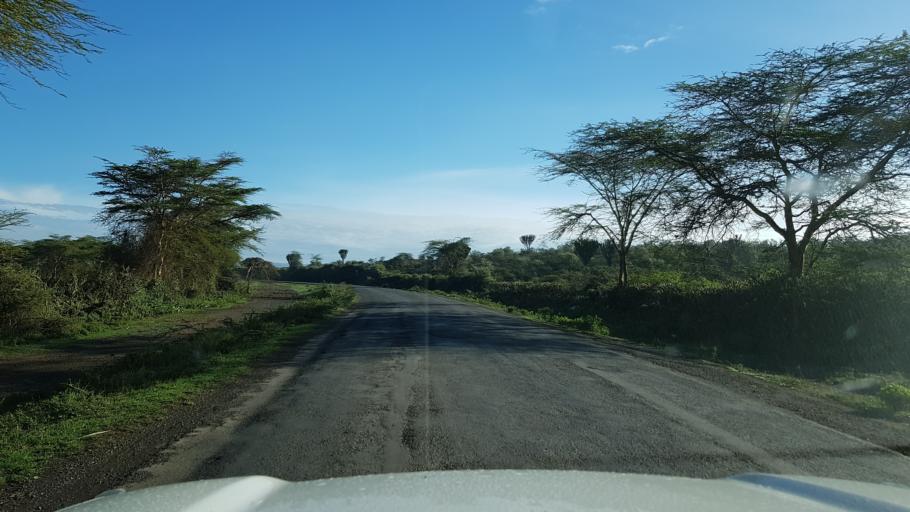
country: KE
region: Nakuru
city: Naivasha
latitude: -0.7892
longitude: 36.4253
